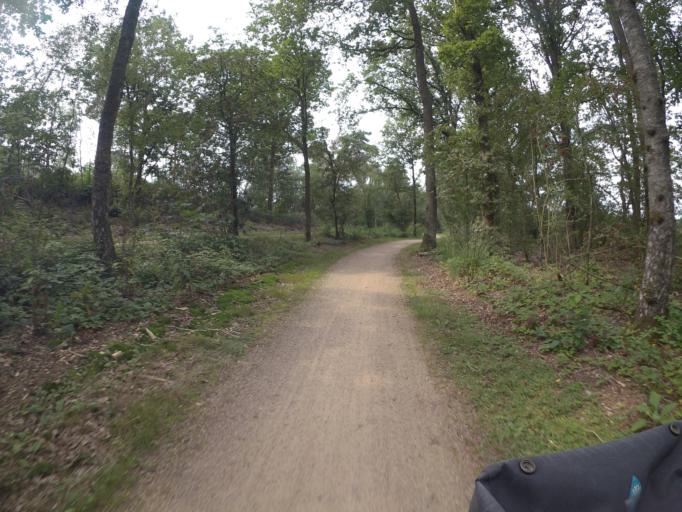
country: NL
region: Limburg
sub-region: Gemeente Bergen
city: Wellerlooi
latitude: 51.5561
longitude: 6.1401
